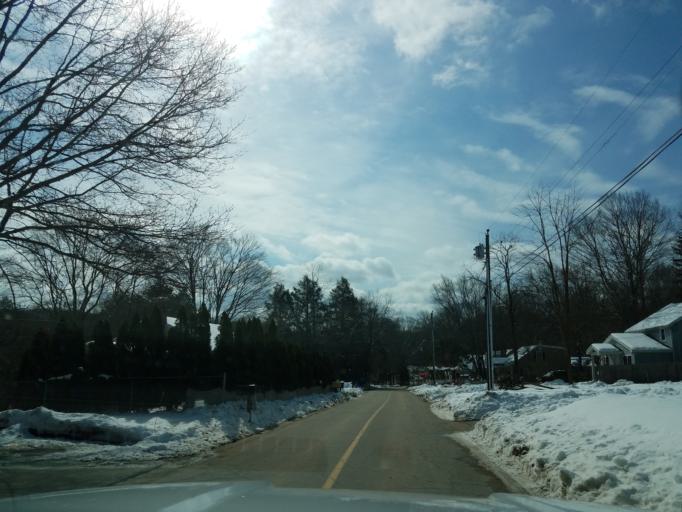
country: US
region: Connecticut
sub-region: Tolland County
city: Hebron
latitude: 41.7134
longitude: -72.3612
